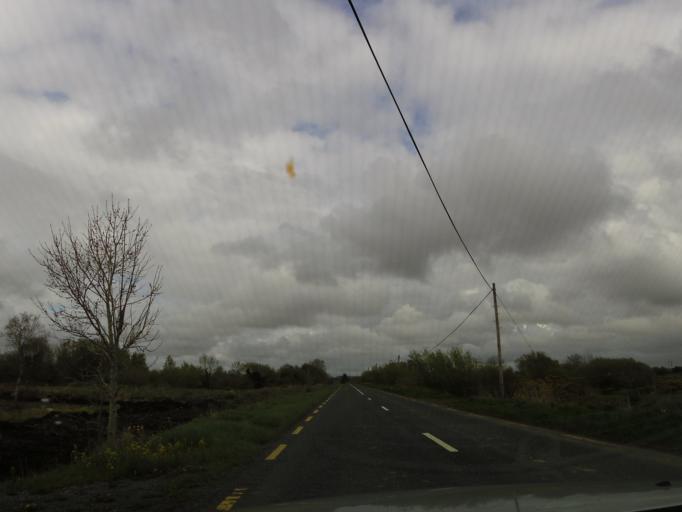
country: IE
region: Connaught
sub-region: Maigh Eo
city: Claremorris
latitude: 53.6922
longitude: -9.0717
